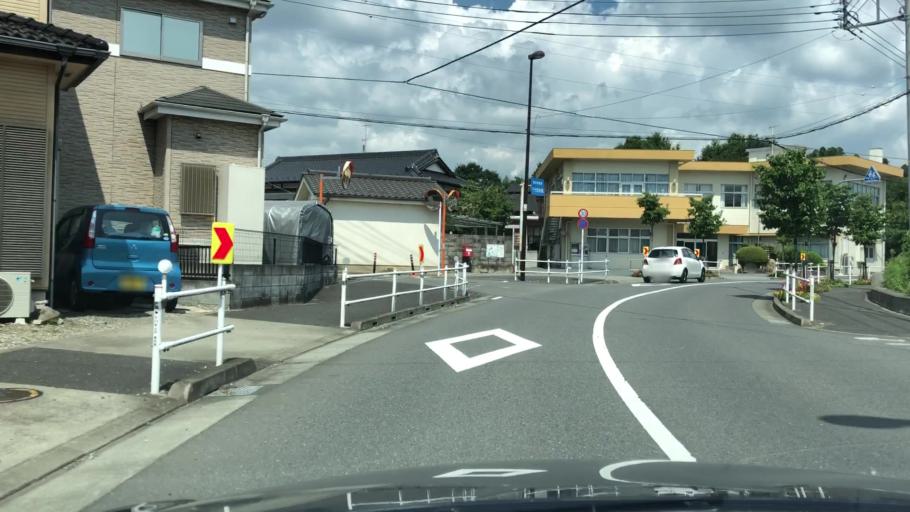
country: JP
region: Tokyo
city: Fussa
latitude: 35.7202
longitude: 139.2782
